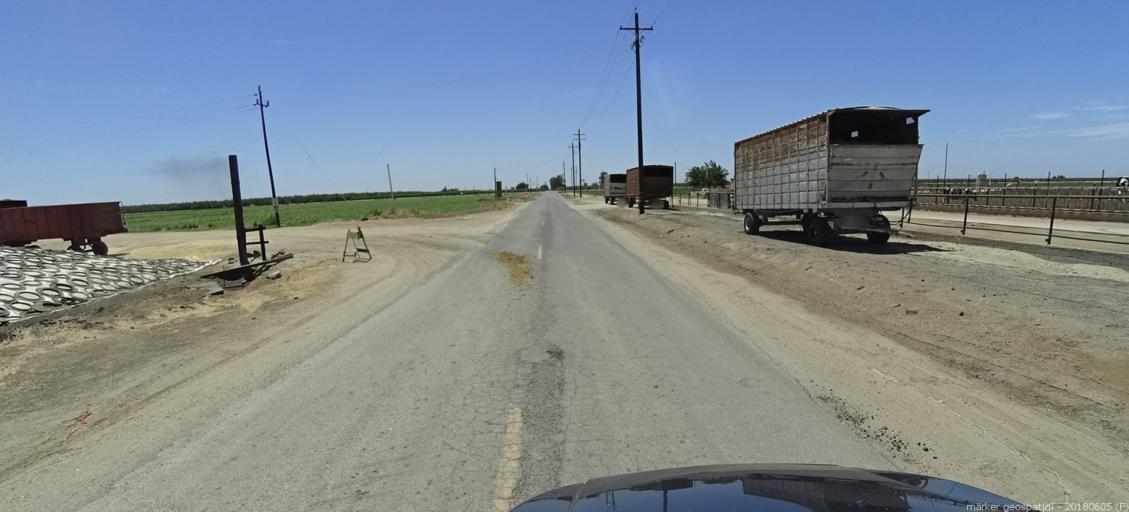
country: US
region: California
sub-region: Madera County
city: Chowchilla
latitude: 37.0880
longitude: -120.3289
